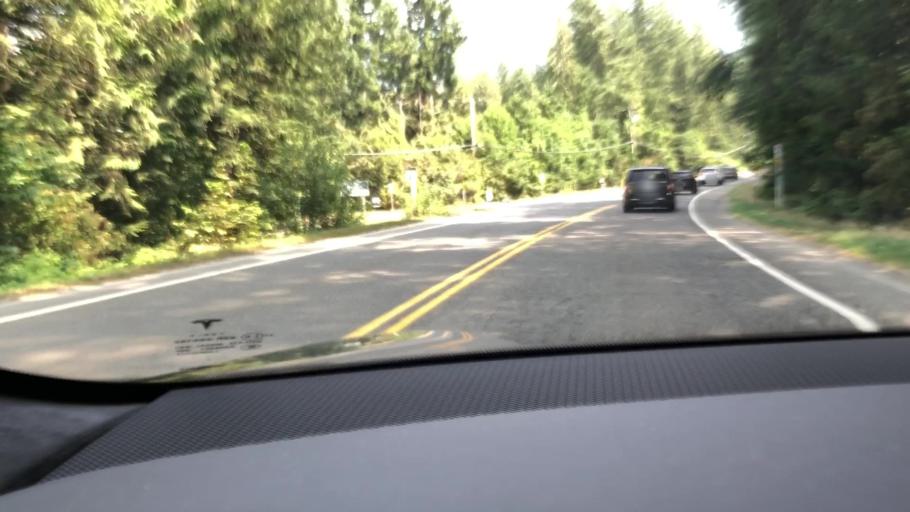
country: CA
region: British Columbia
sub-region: Fraser Valley Regional District
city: Chilliwack
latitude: 49.0743
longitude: -121.9640
